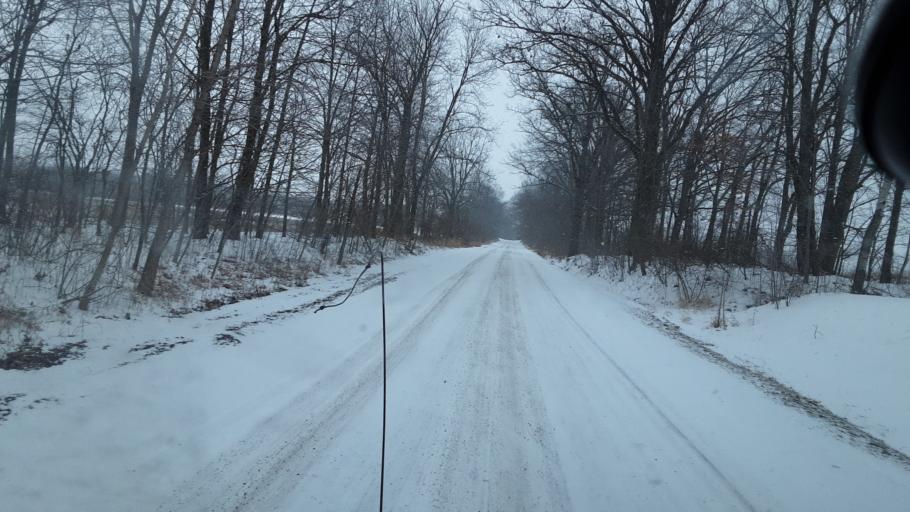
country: US
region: Michigan
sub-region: Ingham County
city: Leslie
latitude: 42.4221
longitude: -84.4602
